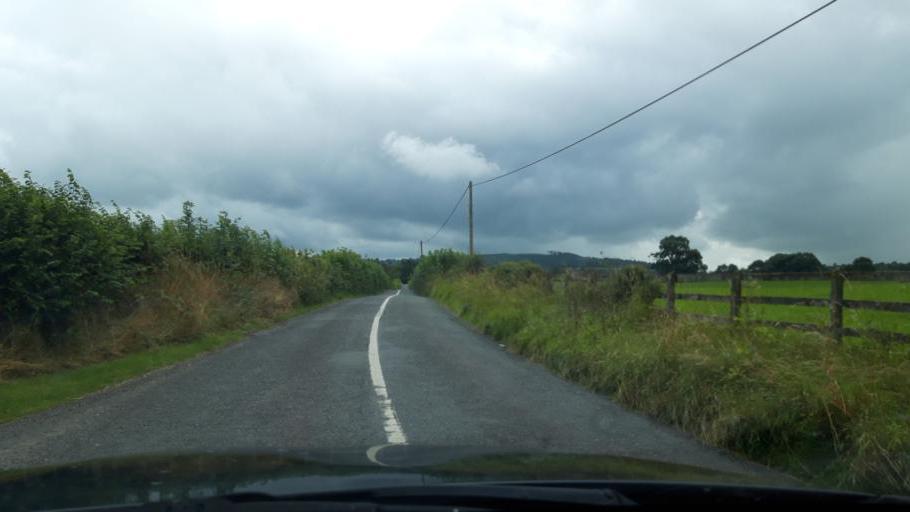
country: IE
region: Munster
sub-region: County Cork
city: Castlemartyr
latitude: 52.1350
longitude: -8.0119
